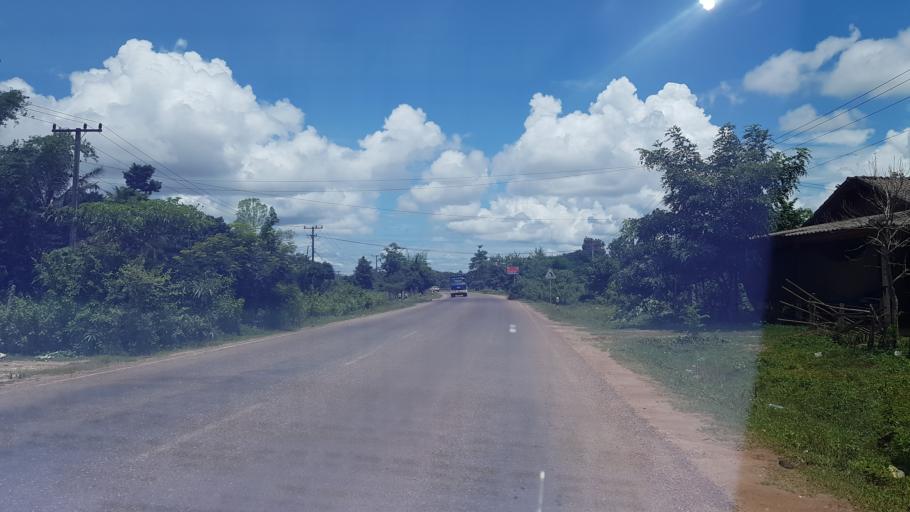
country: LA
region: Vientiane
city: Vientiane
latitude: 18.1073
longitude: 102.5724
